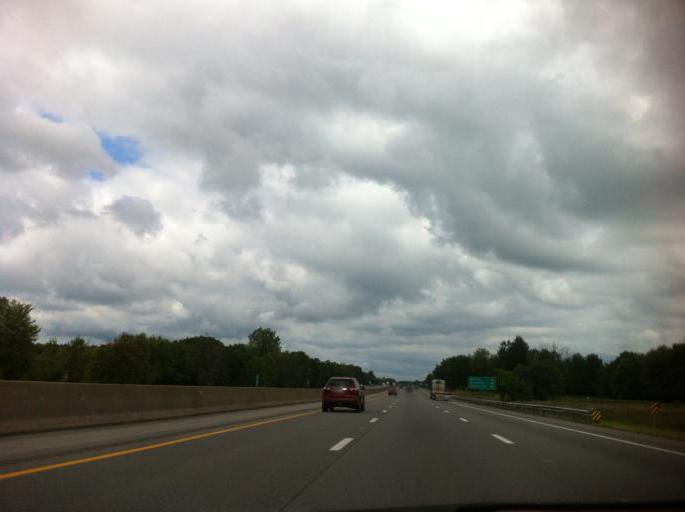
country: US
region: Ohio
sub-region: Trumbull County
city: Lordstown
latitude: 41.1601
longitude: -80.9026
